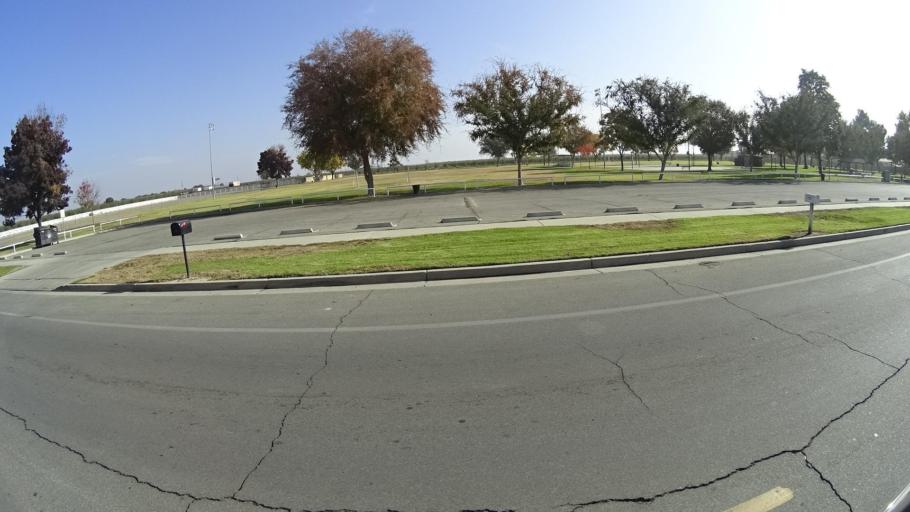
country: US
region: California
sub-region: Kern County
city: McFarland
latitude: 35.6849
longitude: -119.2231
